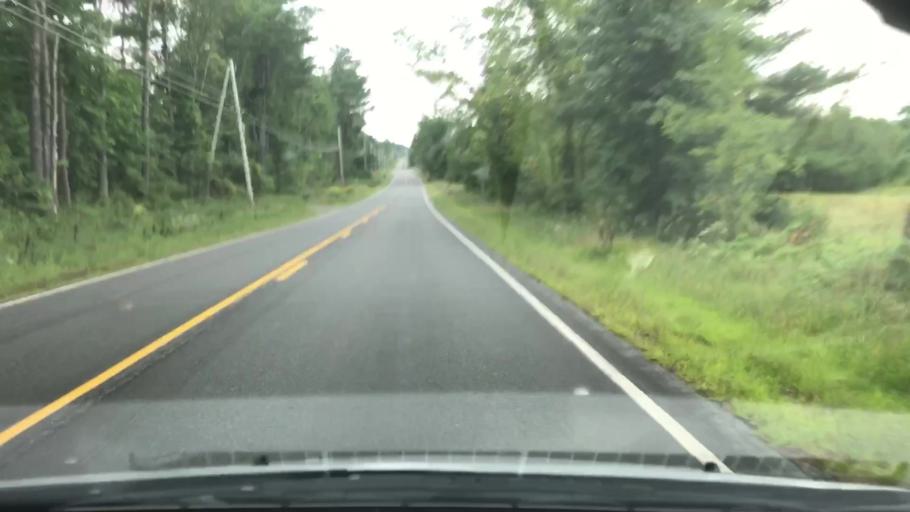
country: US
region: New Hampshire
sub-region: Grafton County
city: Haverhill
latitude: 44.0137
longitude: -72.0685
